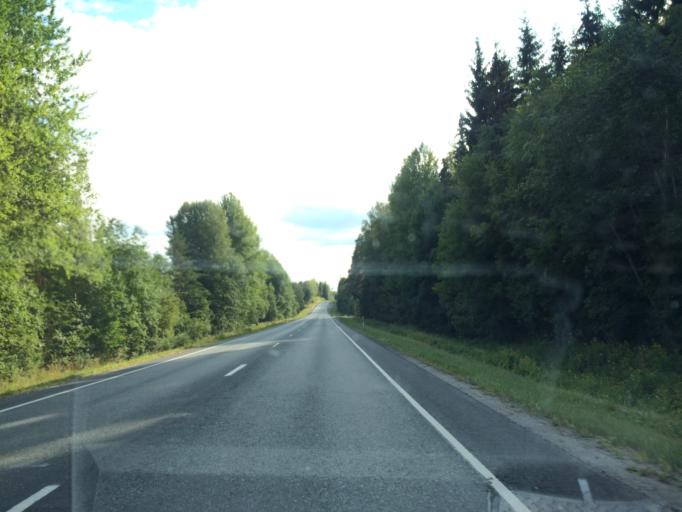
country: FI
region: Haeme
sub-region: Haemeenlinna
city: Haemeenlinna
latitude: 60.9443
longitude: 24.3917
